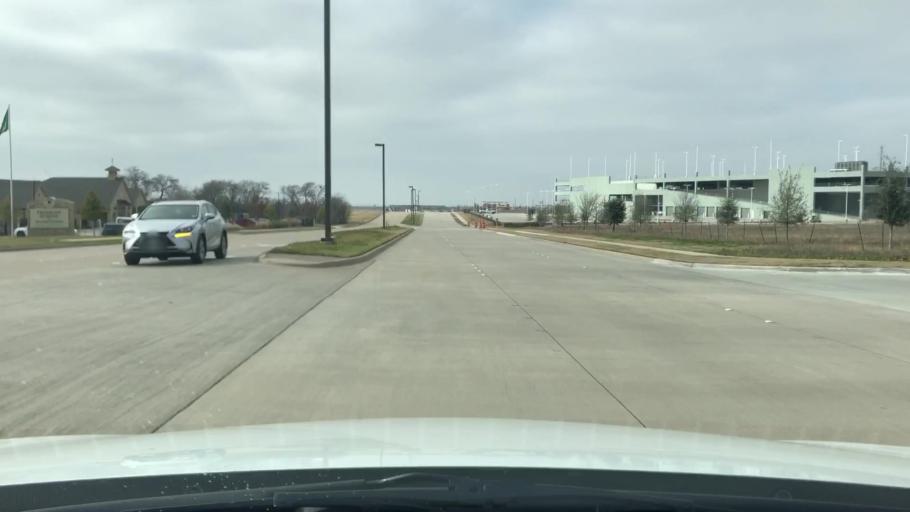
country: US
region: Texas
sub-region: Denton County
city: The Colony
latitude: 33.0803
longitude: -96.8450
